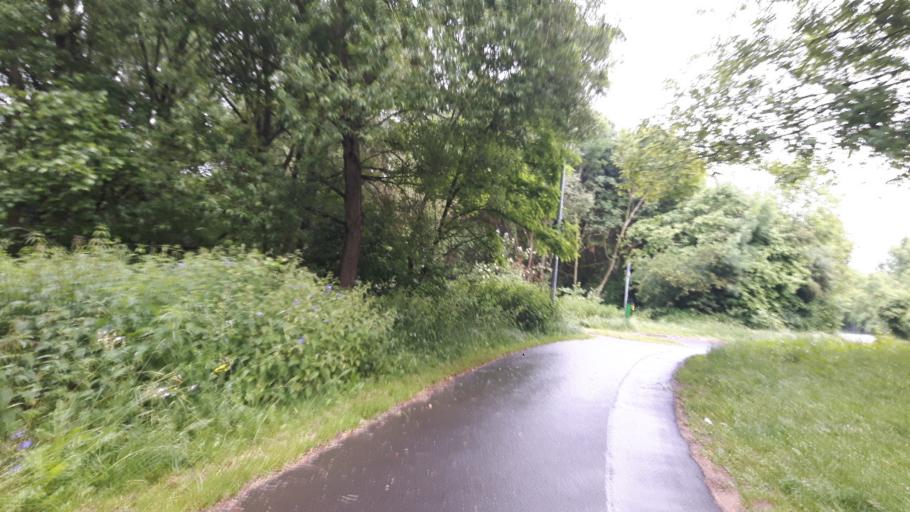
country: DE
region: Bavaria
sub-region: Regierungsbezirk Unterfranken
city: Schweinfurt
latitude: 50.0584
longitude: 10.2314
